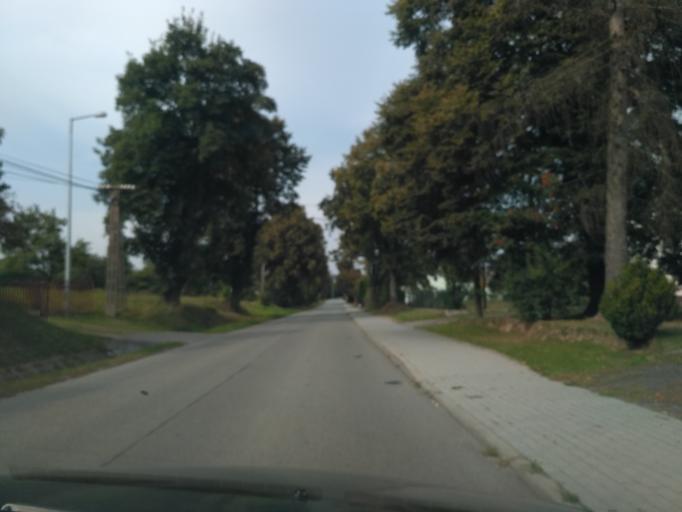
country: PL
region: Subcarpathian Voivodeship
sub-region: Powiat rzeszowski
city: Trzciana
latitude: 50.0678
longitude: 21.8349
